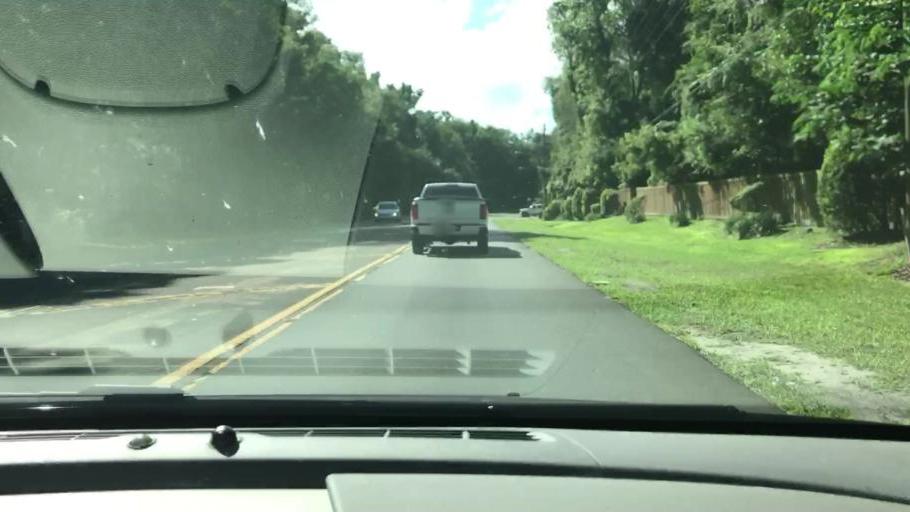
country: US
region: Florida
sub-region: Alachua County
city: Gainesville
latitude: 29.6452
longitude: -82.3997
